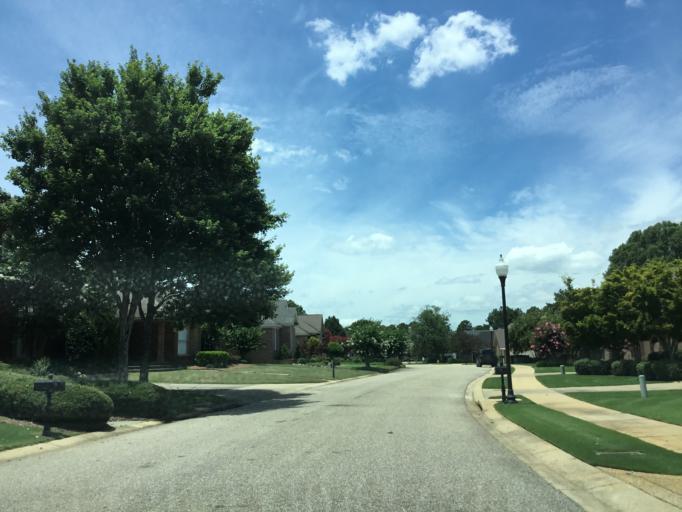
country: US
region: Alabama
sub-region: Montgomery County
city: Pike Road
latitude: 32.3722
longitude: -86.1387
